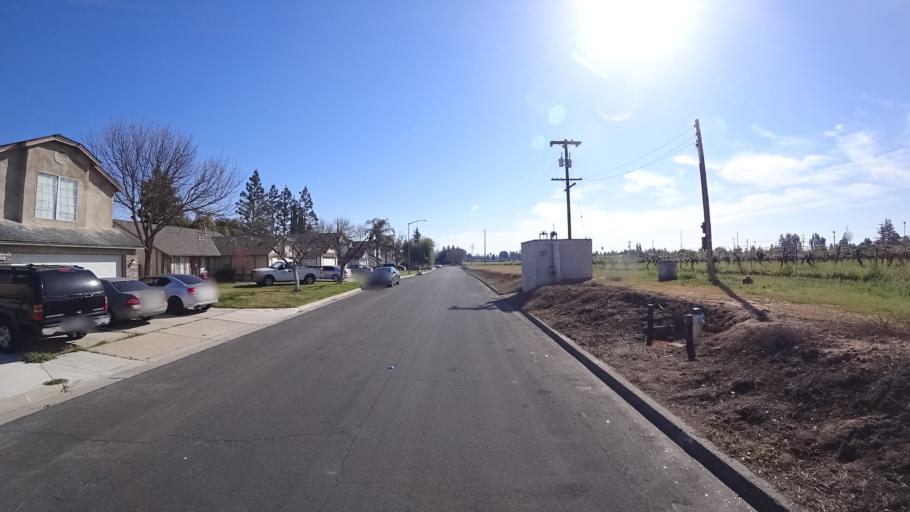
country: US
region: California
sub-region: Fresno County
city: West Park
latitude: 36.7954
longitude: -119.8916
